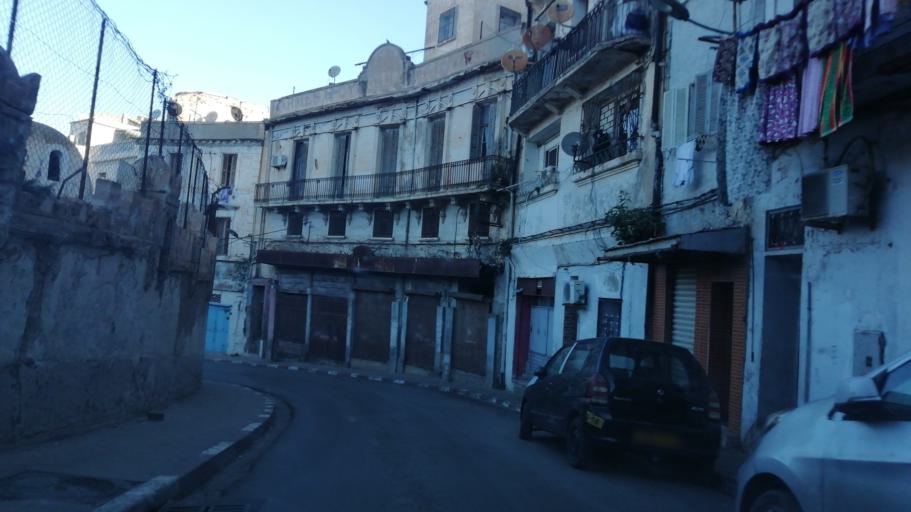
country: DZ
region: Oran
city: Oran
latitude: 35.7050
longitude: -0.6498
